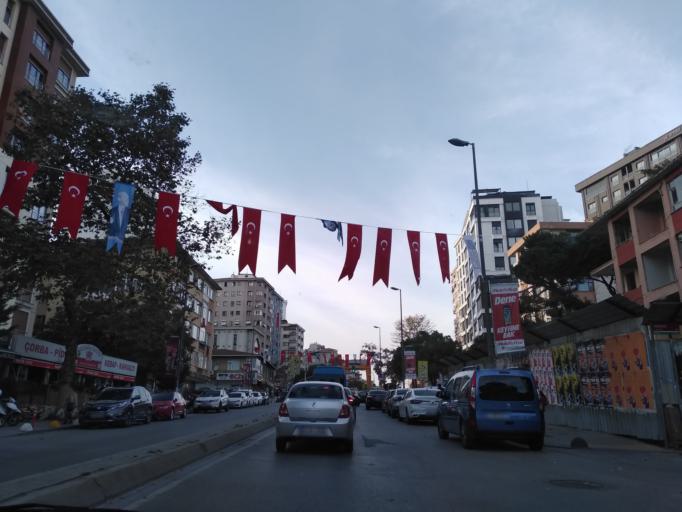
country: TR
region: Istanbul
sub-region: Atasehir
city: Atasehir
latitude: 40.9649
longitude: 29.0882
